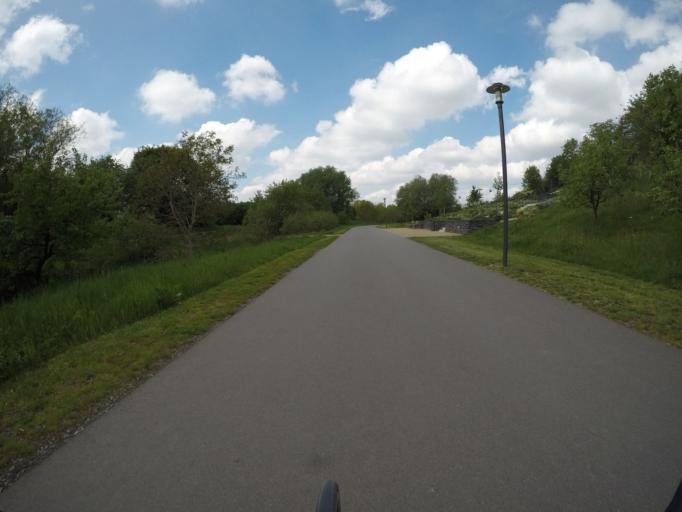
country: DE
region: Berlin
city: Marzahn
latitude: 52.5320
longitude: 13.5789
